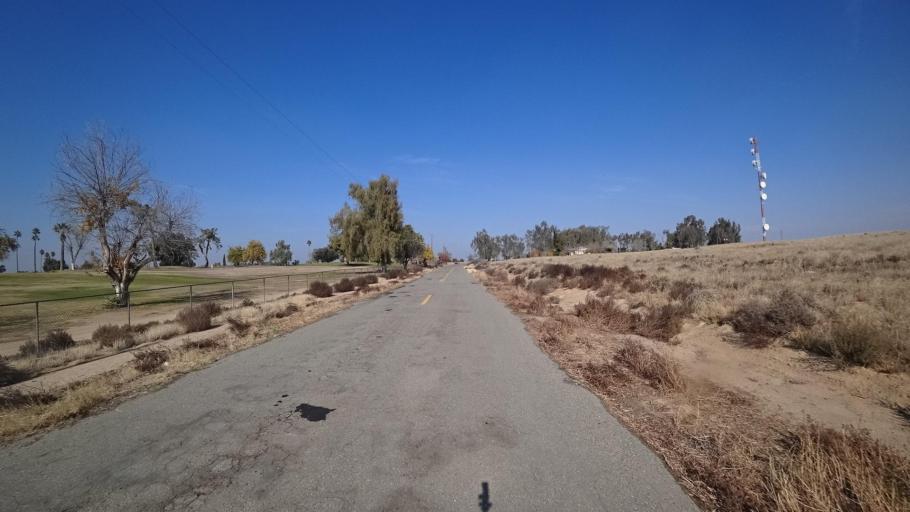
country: US
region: California
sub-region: Kern County
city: Oildale
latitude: 35.5210
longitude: -119.1087
